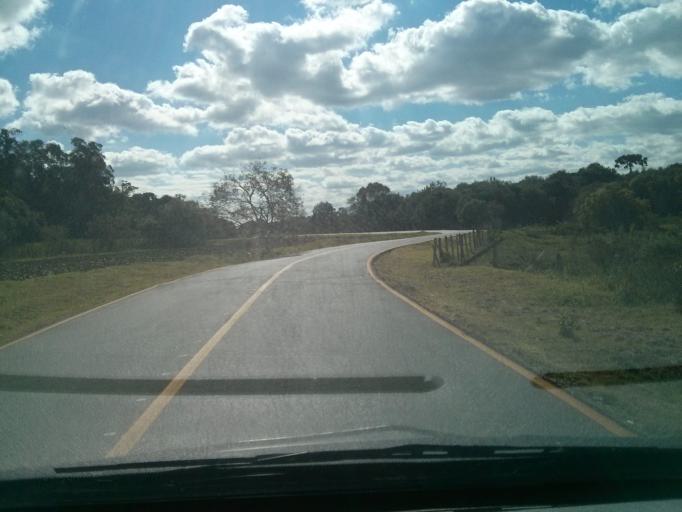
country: BR
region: Parana
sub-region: Sao Jose Dos Pinhais
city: Sao Jose dos Pinhais
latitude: -25.5590
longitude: -49.2266
